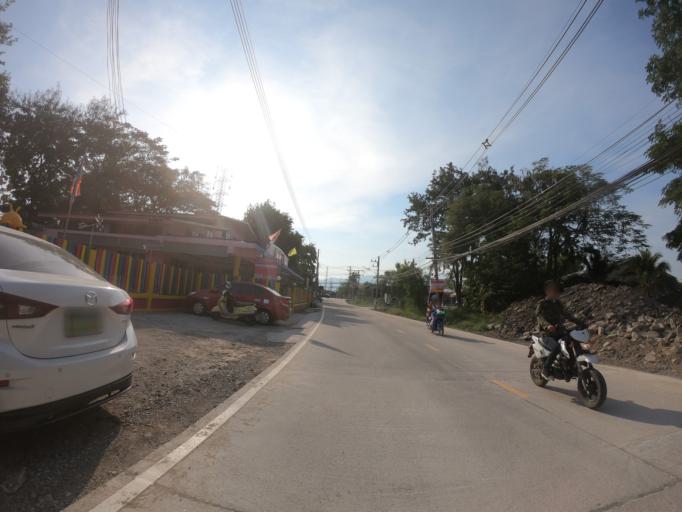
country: TH
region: Chiang Mai
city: Chiang Mai
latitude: 18.8191
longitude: 99.0126
